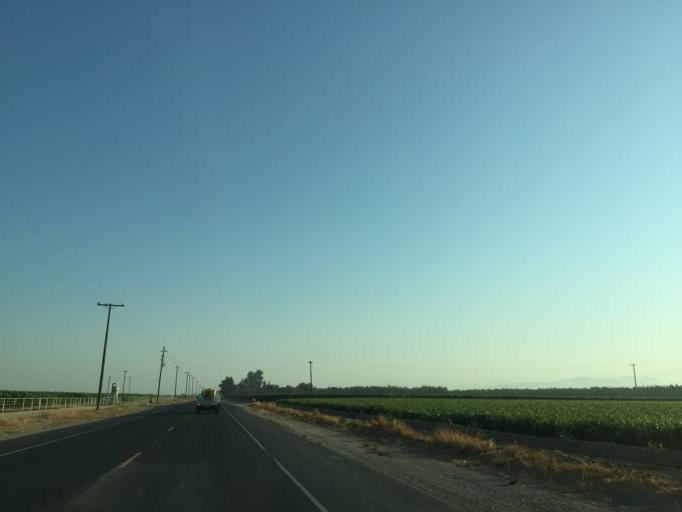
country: US
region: California
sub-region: Tulare County
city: Ivanhoe
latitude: 36.4163
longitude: -119.2961
